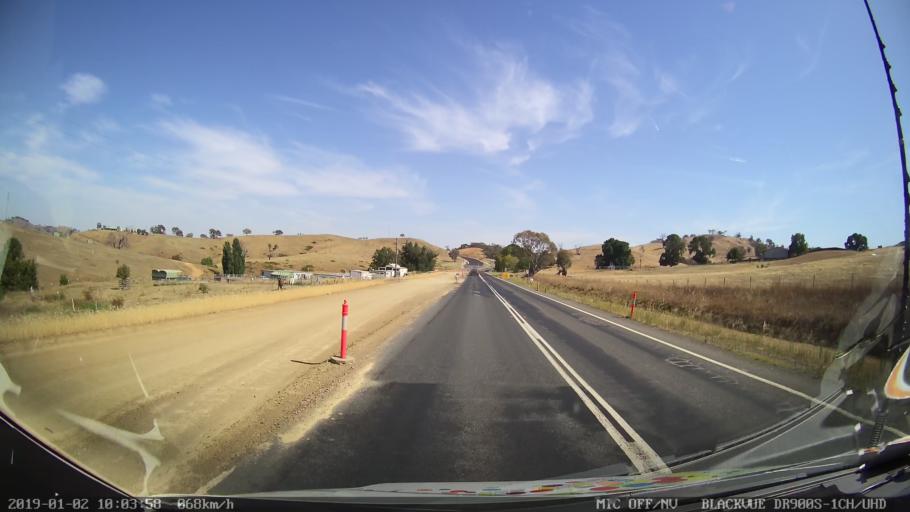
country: AU
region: New South Wales
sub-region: Gundagai
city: Gundagai
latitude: -35.1724
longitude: 148.1245
